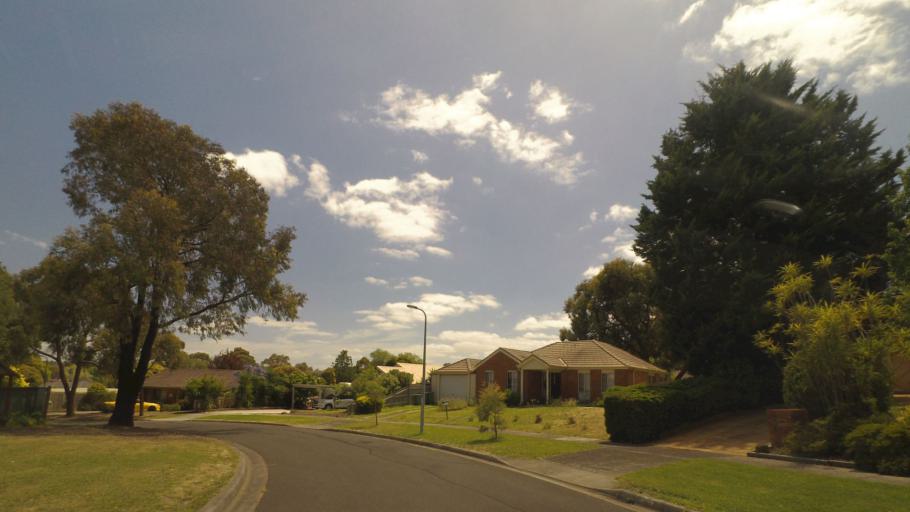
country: AU
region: Victoria
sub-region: Maroondah
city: Bayswater North
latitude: -37.8257
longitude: 145.2965
